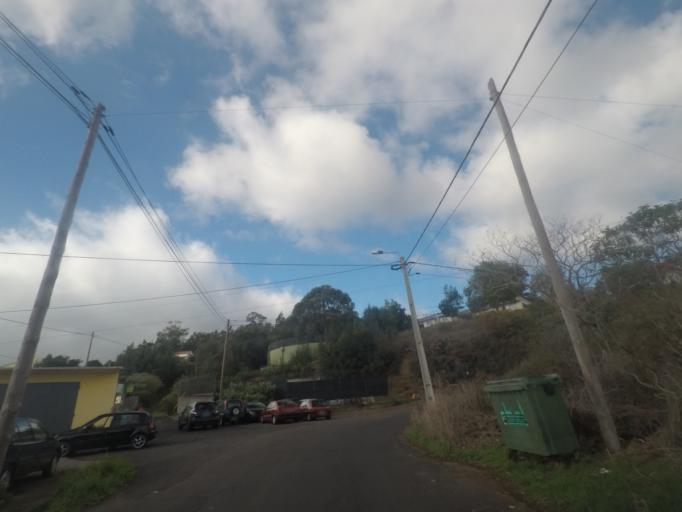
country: PT
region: Madeira
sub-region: Santa Cruz
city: Camacha
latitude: 32.6633
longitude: -16.8658
